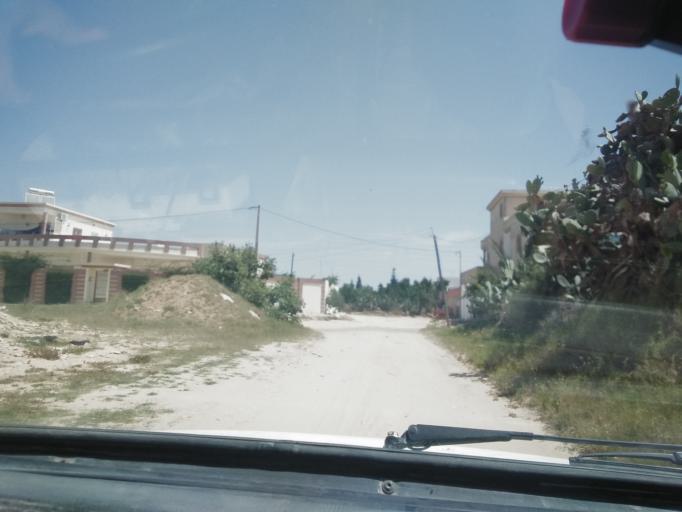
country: TN
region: Safaqis
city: Al Qarmadah
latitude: 34.8040
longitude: 10.7759
